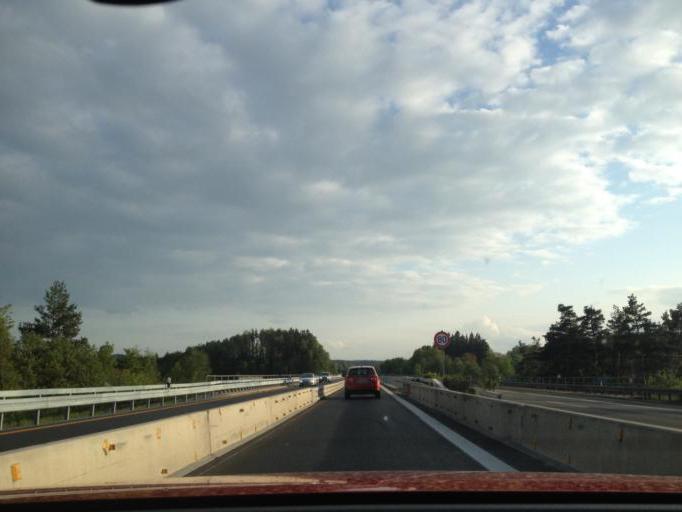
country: DE
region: Bavaria
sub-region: Upper Palatinate
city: Windischeschenbach
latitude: 49.7862
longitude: 12.1679
